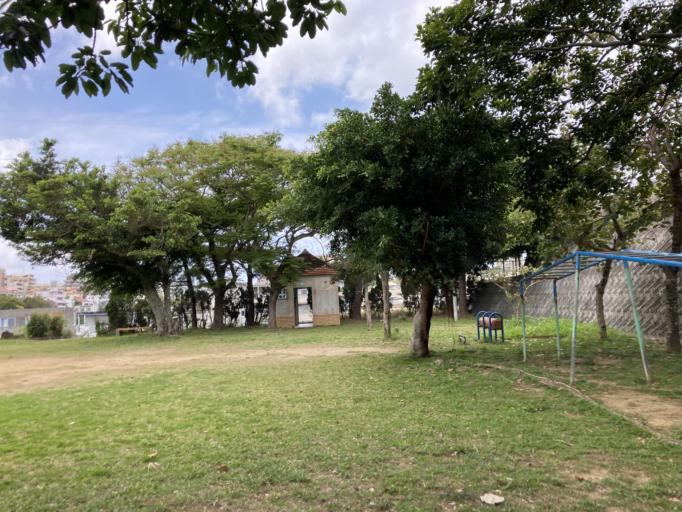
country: JP
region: Okinawa
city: Tomigusuku
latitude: 26.1918
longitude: 127.6740
